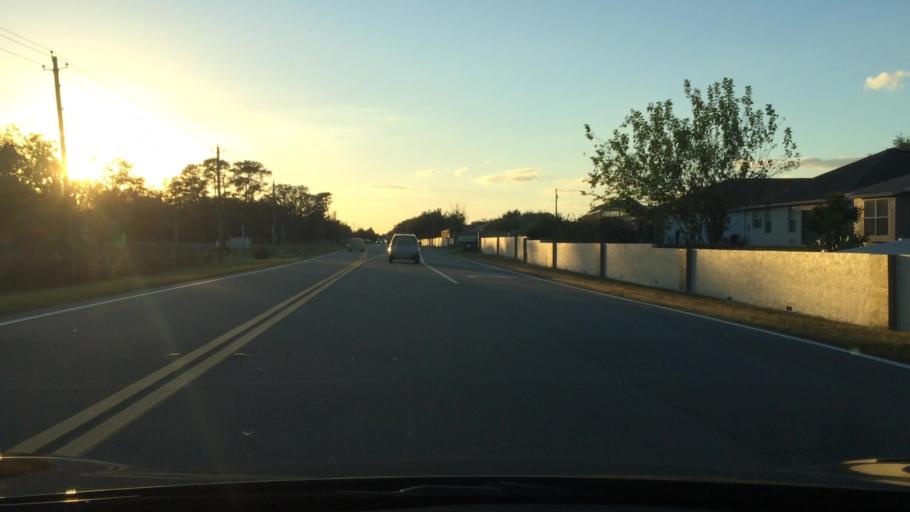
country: US
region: Florida
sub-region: Hillsborough County
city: Lutz
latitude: 28.1713
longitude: -82.4092
